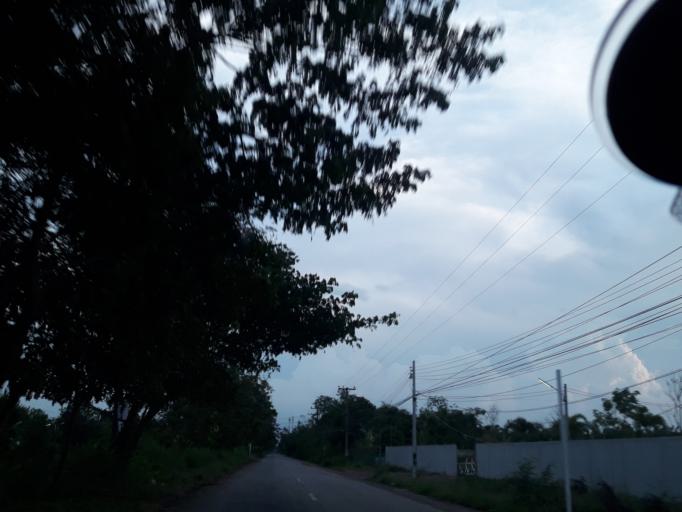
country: TH
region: Pathum Thani
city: Nong Suea
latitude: 14.1168
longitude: 100.8685
